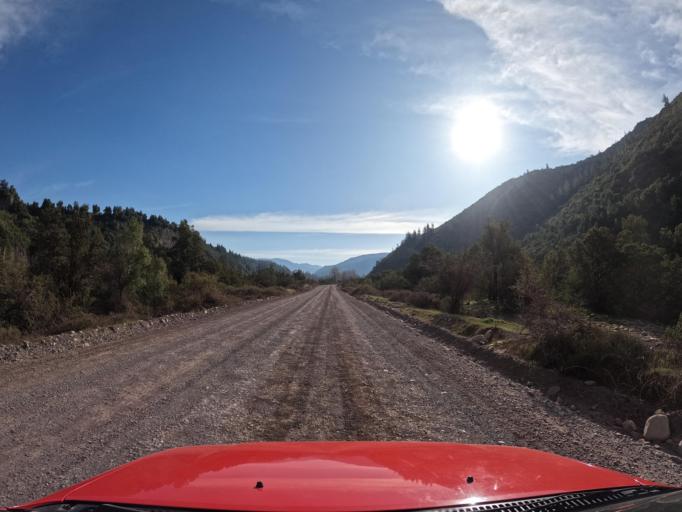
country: CL
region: O'Higgins
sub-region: Provincia de Colchagua
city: Chimbarongo
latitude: -34.9993
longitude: -70.7982
